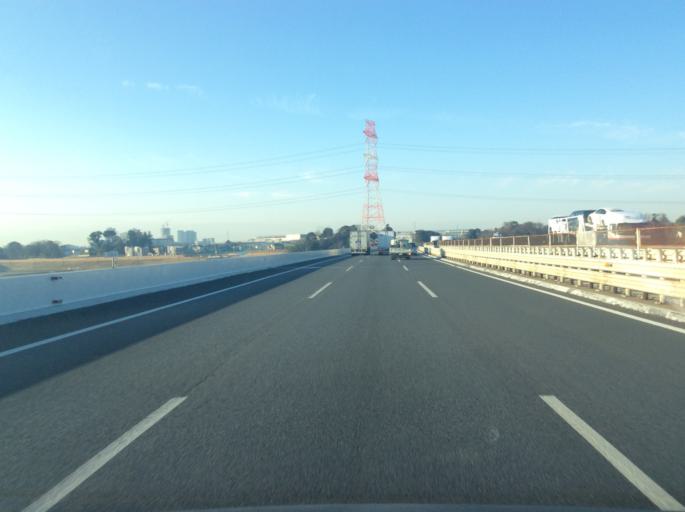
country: JP
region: Ibaraki
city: Moriya
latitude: 35.9239
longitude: 139.9587
